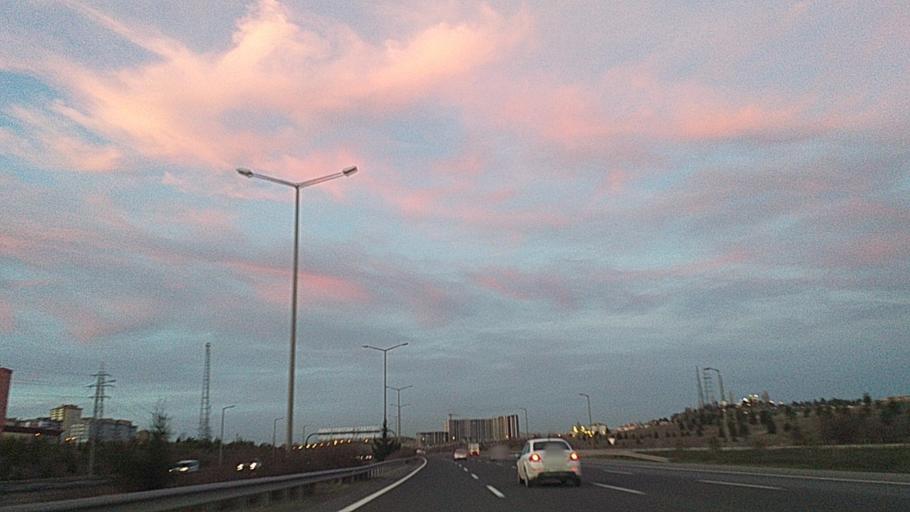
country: TR
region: Ankara
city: Etimesgut
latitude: 39.9698
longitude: 32.6321
